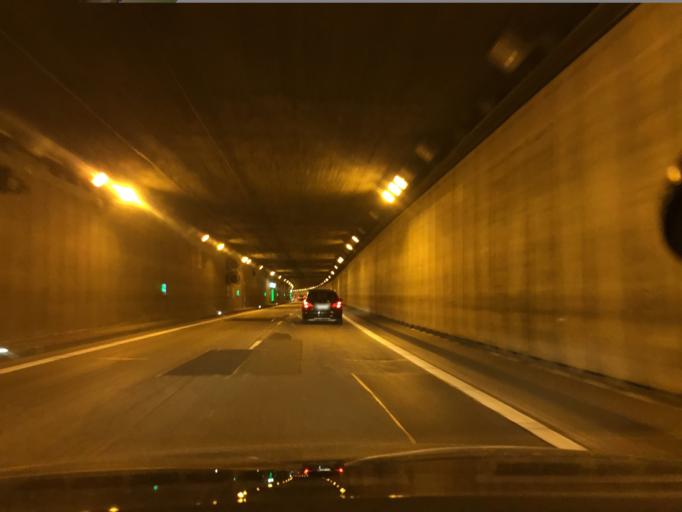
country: DE
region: North Rhine-Westphalia
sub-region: Regierungsbezirk Dusseldorf
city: Dusseldorf
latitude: 51.2304
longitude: 6.7388
